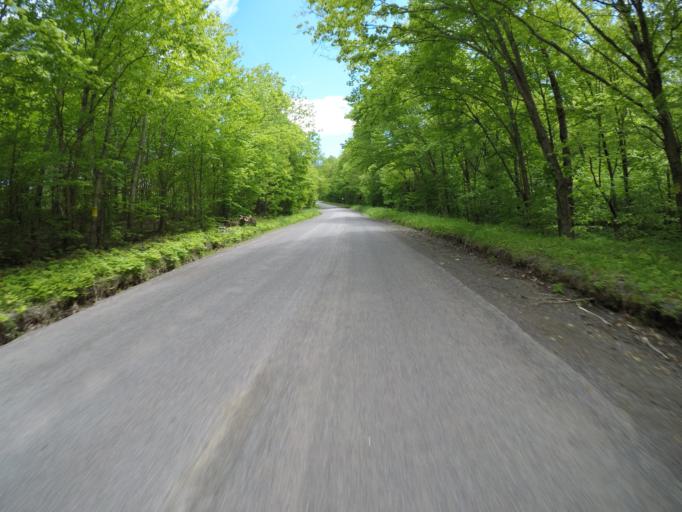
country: US
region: New York
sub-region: Delaware County
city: Stamford
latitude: 42.2786
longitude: -74.5032
